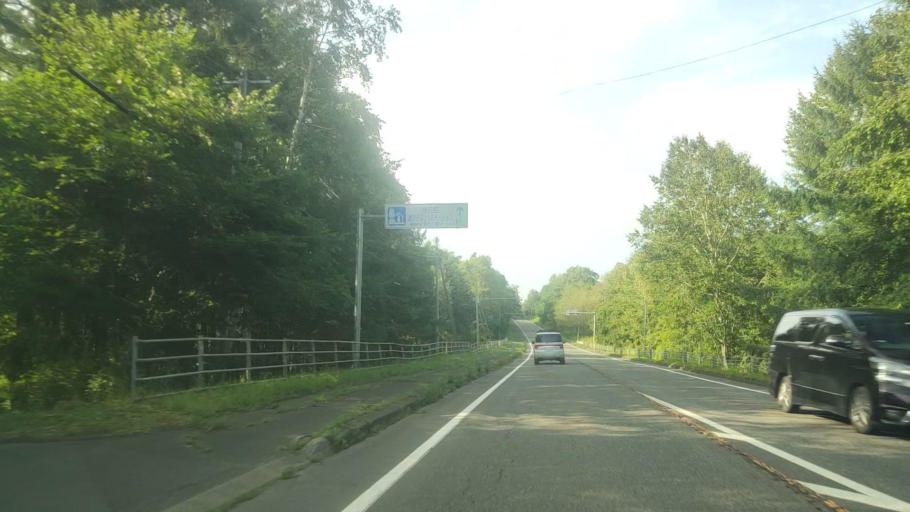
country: JP
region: Hokkaido
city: Chitose
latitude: 42.8674
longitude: 141.8226
